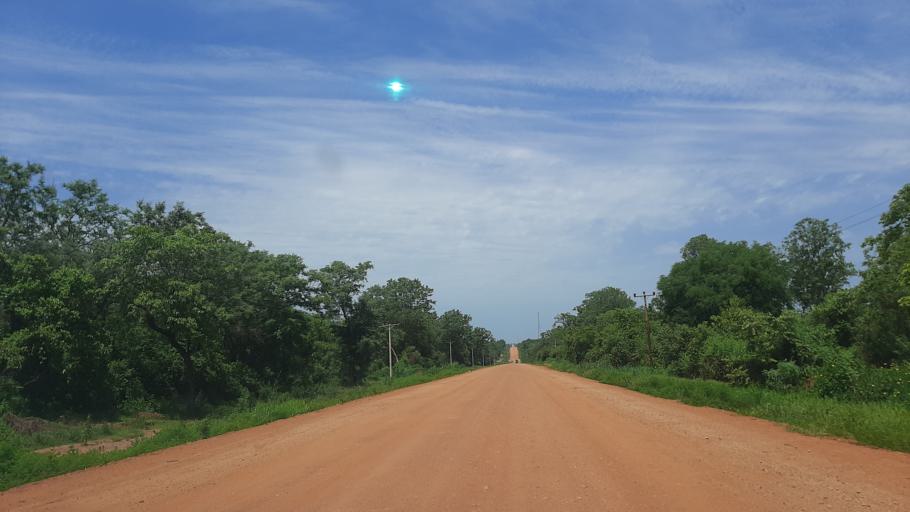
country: ET
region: Gambela
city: Gambela
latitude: 8.0747
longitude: 34.5894
